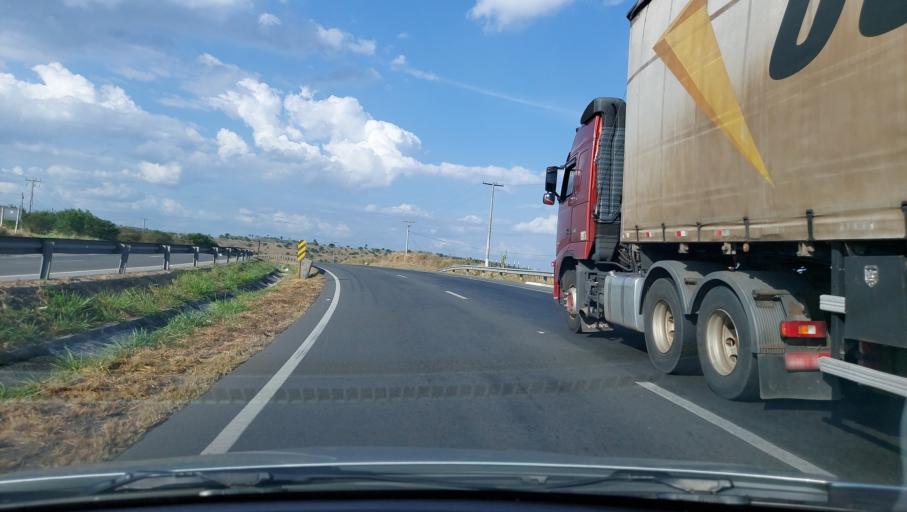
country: BR
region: Bahia
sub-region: Feira De Santana
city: Feira de Santana
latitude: -12.3422
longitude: -39.0824
